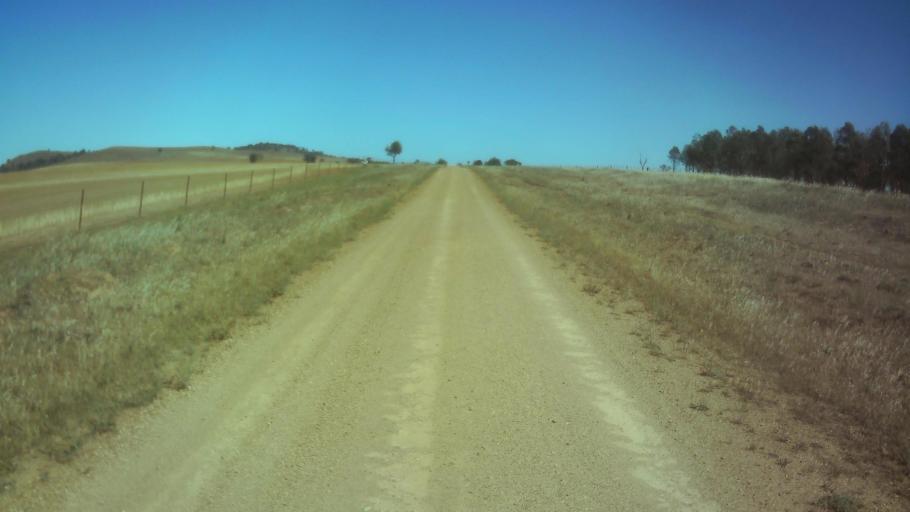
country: AU
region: New South Wales
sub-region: Weddin
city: Grenfell
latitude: -33.9676
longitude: 148.3132
